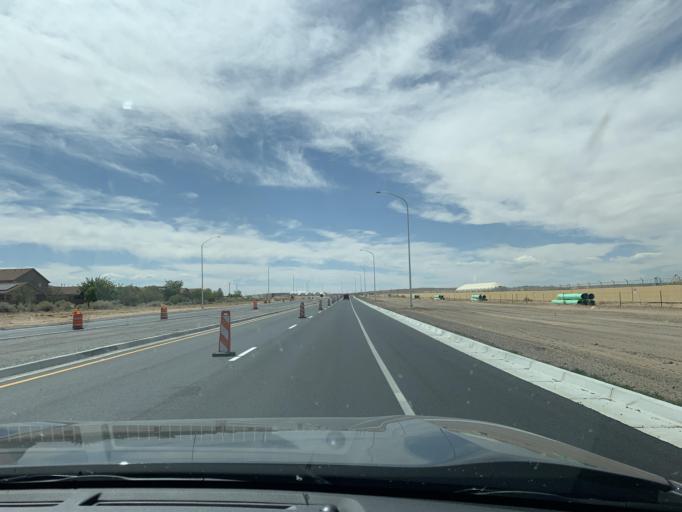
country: US
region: New Mexico
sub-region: Valencia County
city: Los Lunas
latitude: 34.8190
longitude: -106.7764
